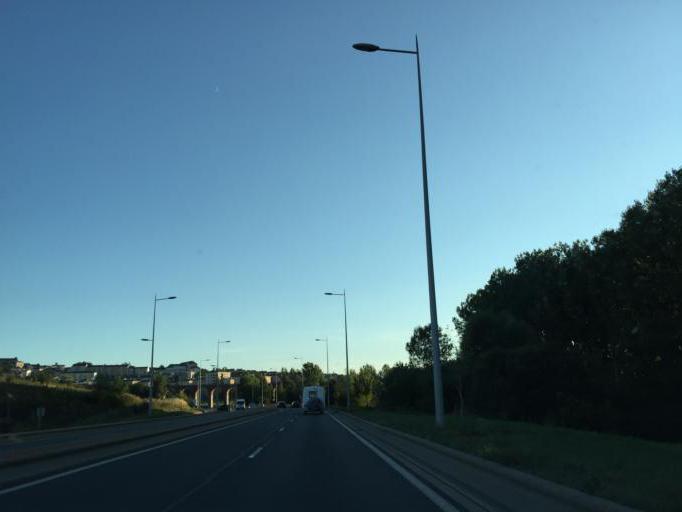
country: FR
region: Midi-Pyrenees
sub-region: Departement de l'Aveyron
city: Rodez
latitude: 44.3676
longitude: 2.5796
